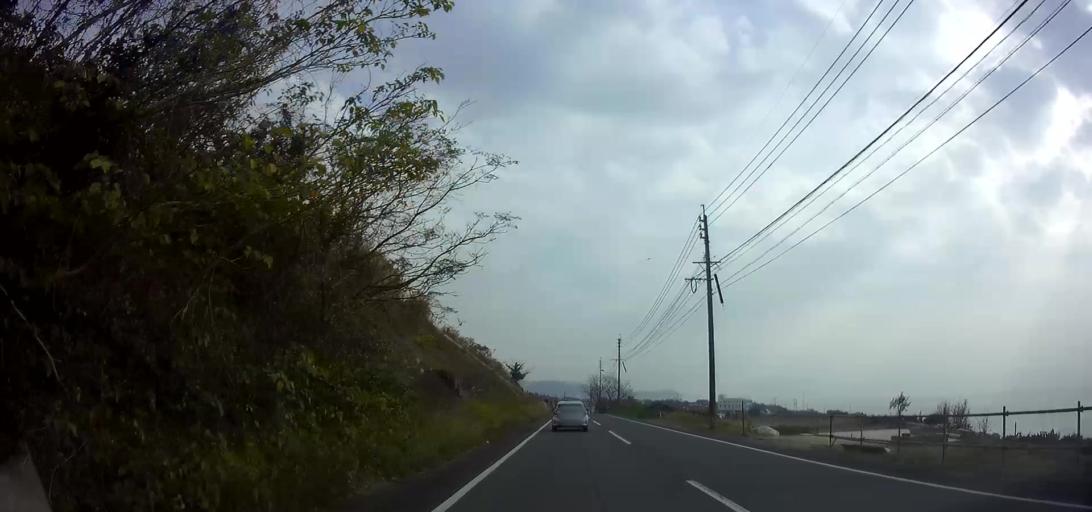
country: JP
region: Nagasaki
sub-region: Isahaya-shi
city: Isahaya
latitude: 32.7913
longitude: 130.0606
